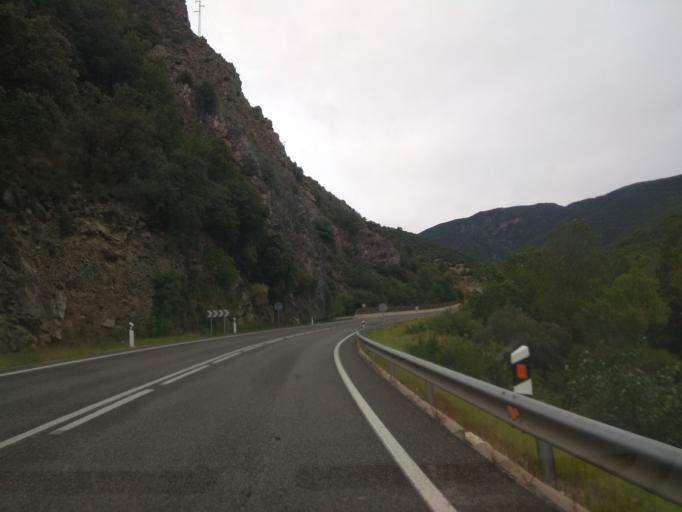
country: ES
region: Catalonia
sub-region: Provincia de Lleida
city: Alas i Cerc
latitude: 42.3593
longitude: 1.5577
